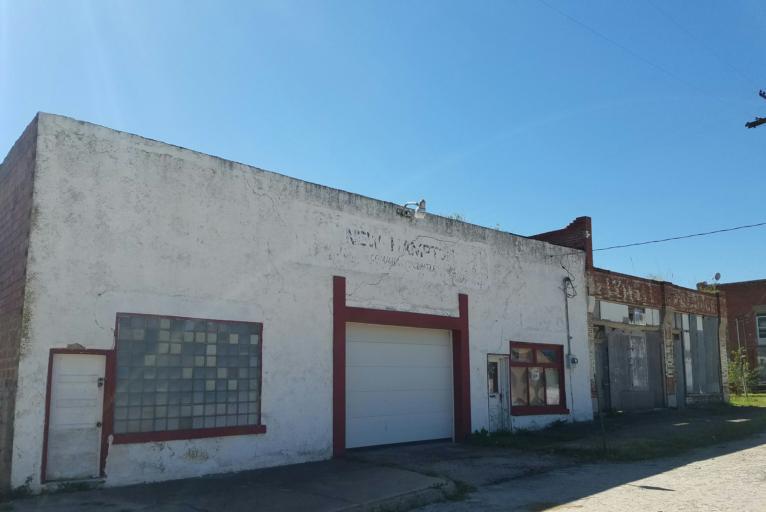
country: US
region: Missouri
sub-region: Gentry County
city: Albany
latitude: 40.2631
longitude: -94.1950
